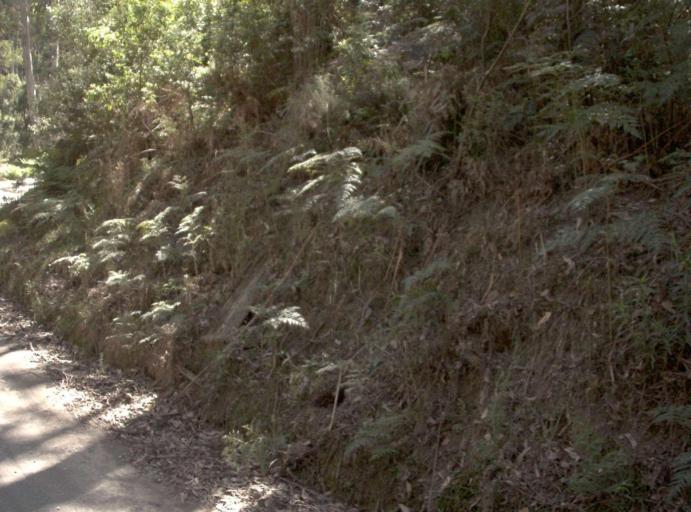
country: AU
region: New South Wales
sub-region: Bombala
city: Bombala
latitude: -37.2453
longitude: 148.7531
